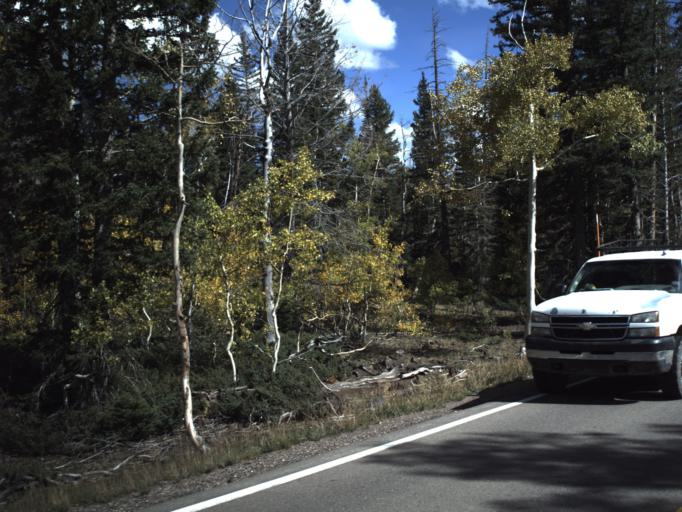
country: US
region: Utah
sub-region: Iron County
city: Parowan
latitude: 37.5244
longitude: -112.7424
